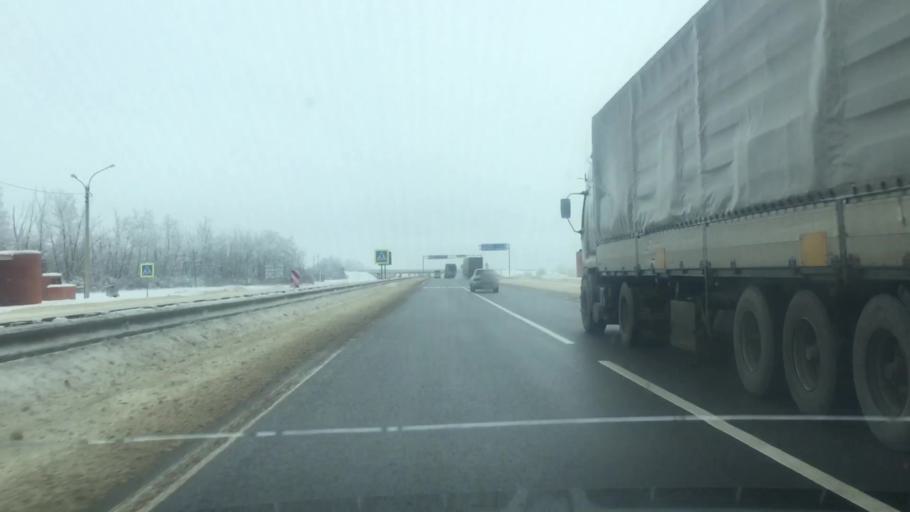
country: RU
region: Tula
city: Kazachka
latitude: 53.3047
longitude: 38.1785
